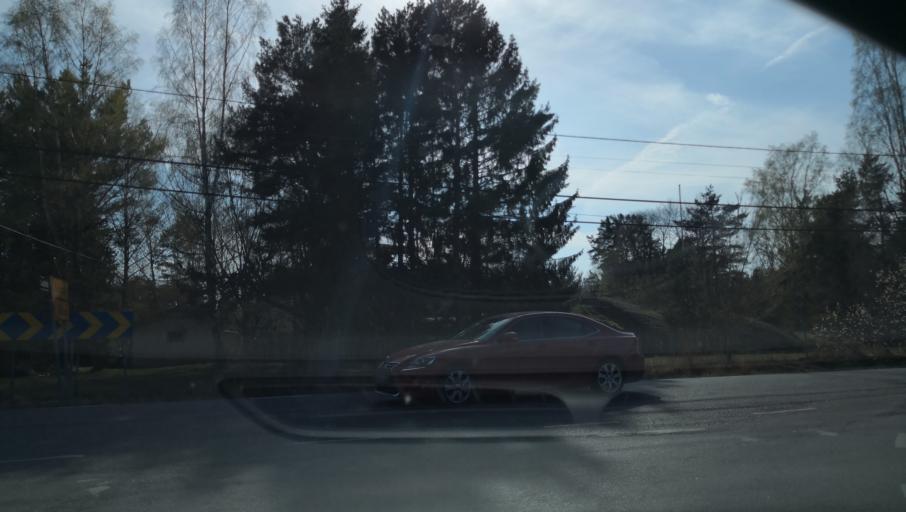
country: SE
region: Stockholm
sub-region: Varmdo Kommun
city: Holo
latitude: 59.2961
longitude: 18.6145
